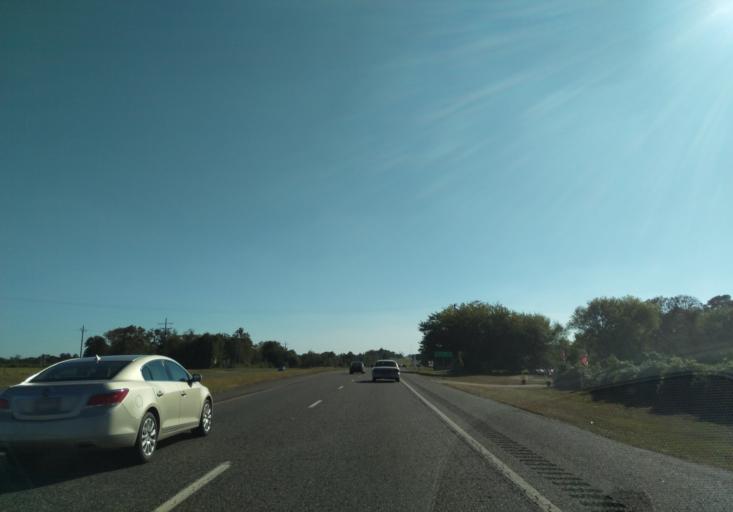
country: US
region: Texas
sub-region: Waller County
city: Hempstead
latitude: 30.2062
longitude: -96.0589
